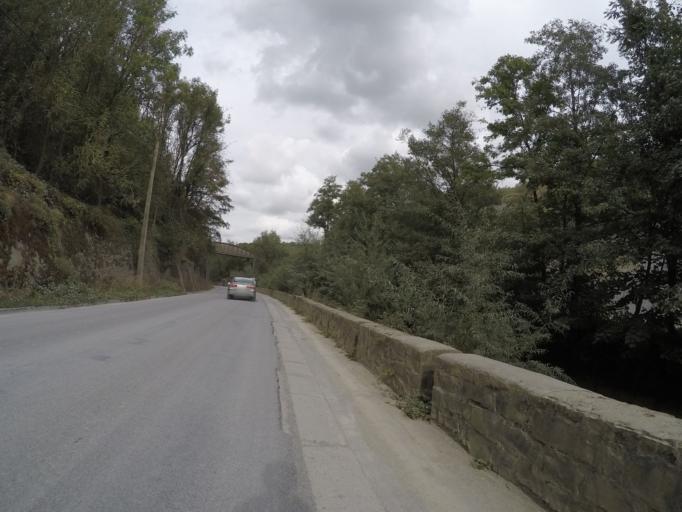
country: BE
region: Wallonia
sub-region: Province de Namur
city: Yvoir
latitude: 50.3290
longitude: 4.8962
